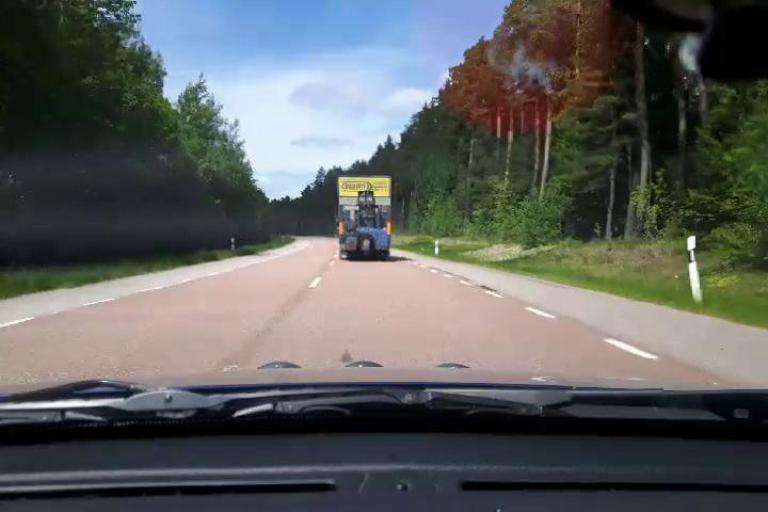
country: SE
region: Uppsala
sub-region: Osthammars Kommun
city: Bjorklinge
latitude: 60.1428
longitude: 17.5031
